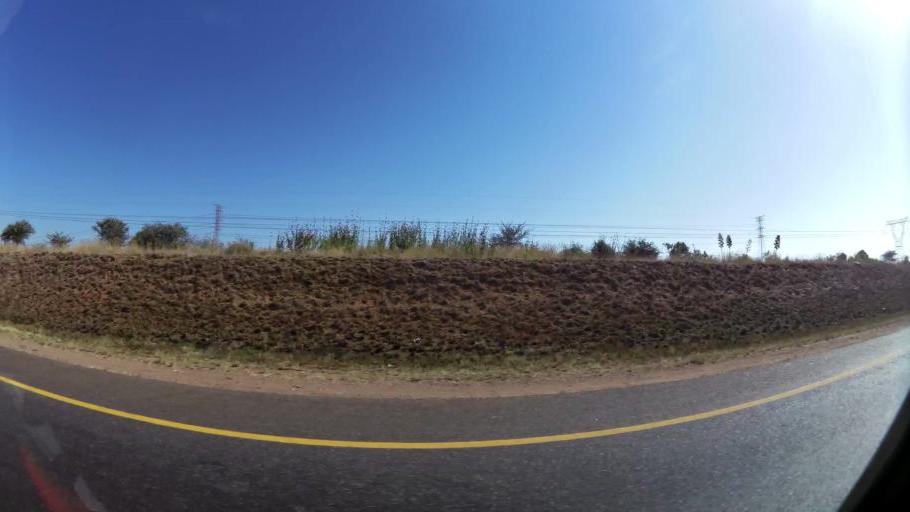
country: ZA
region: Gauteng
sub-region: City of Tshwane Metropolitan Municipality
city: Mabopane
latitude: -25.5436
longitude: 28.1116
